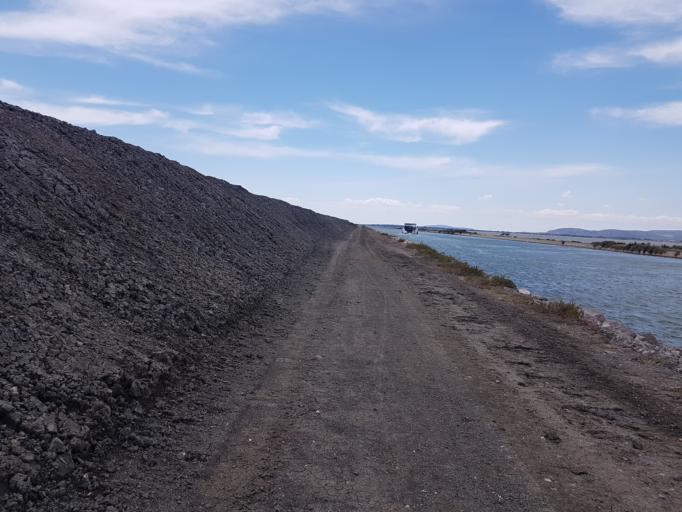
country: FR
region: Languedoc-Roussillon
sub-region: Departement de l'Herault
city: Villeneuve-les-Maguelone
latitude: 43.5021
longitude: 3.8612
